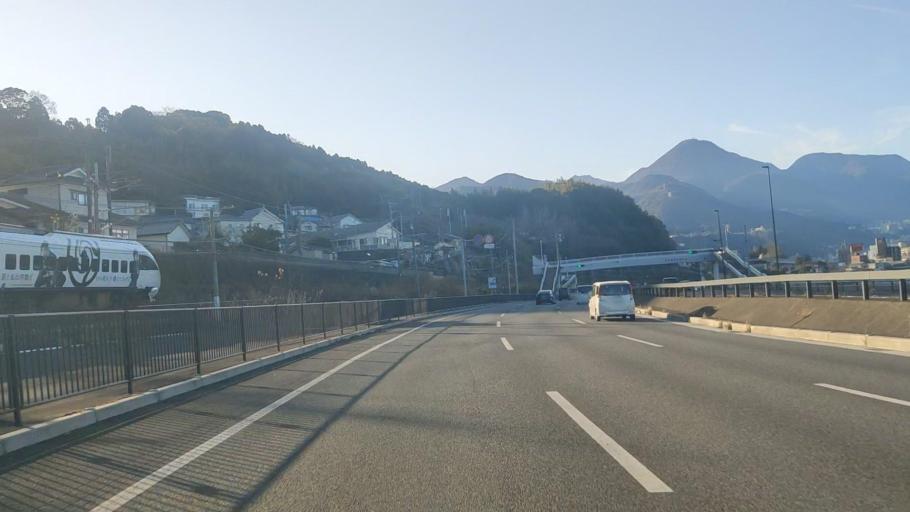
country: JP
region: Oita
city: Beppu
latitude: 33.2648
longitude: 131.5195
